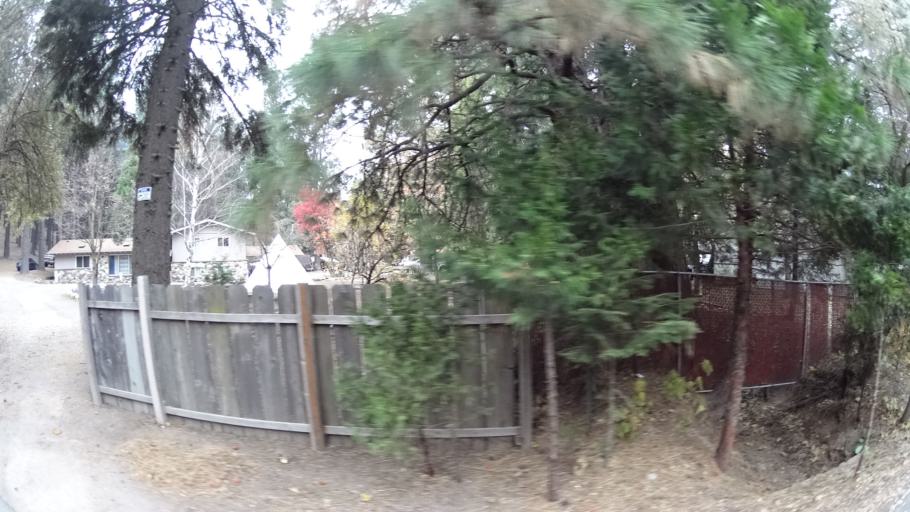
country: US
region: California
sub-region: Siskiyou County
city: Weed
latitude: 41.4128
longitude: -122.3858
